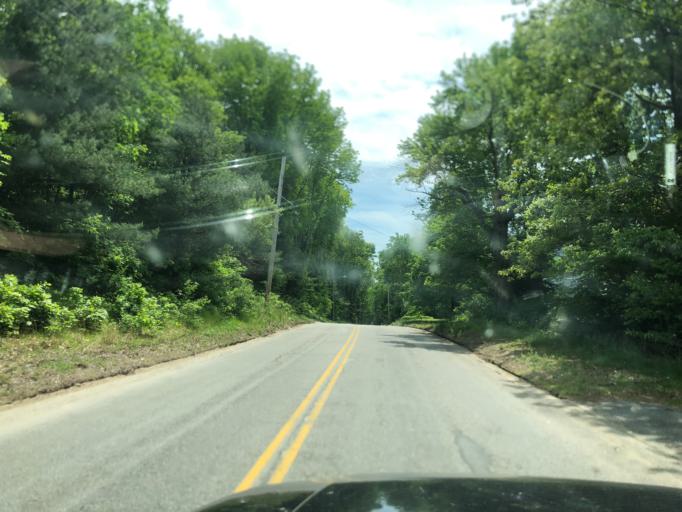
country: US
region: Connecticut
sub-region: Windham County
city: North Grosvenor Dale
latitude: 41.9805
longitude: -71.8905
